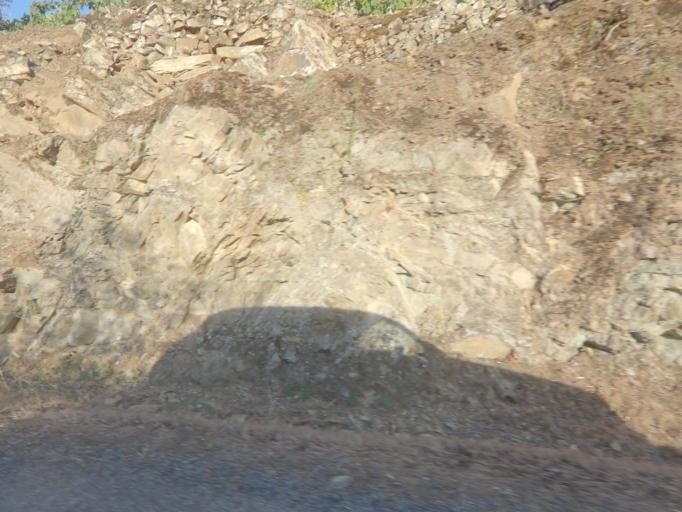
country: PT
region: Viseu
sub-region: Armamar
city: Armamar
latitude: 41.1774
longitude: -7.6902
